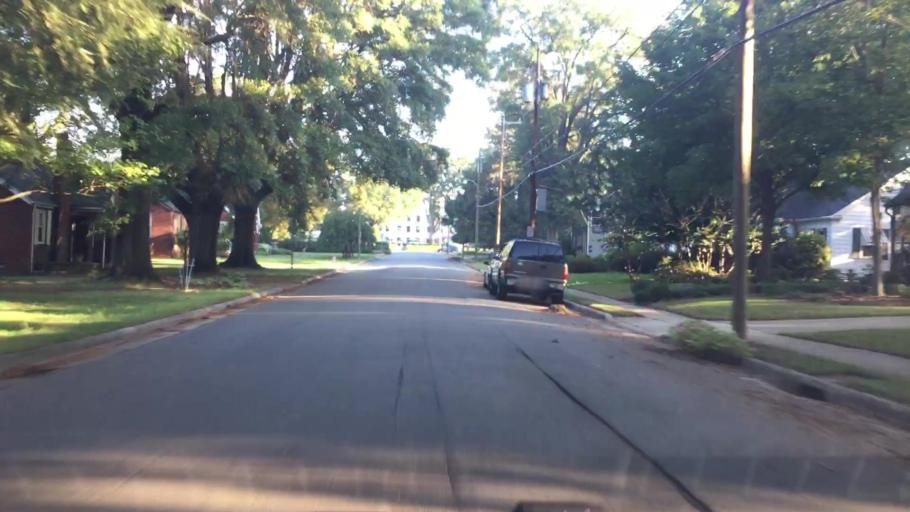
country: US
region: North Carolina
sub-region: Iredell County
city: Mooresville
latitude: 35.5773
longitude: -80.8040
